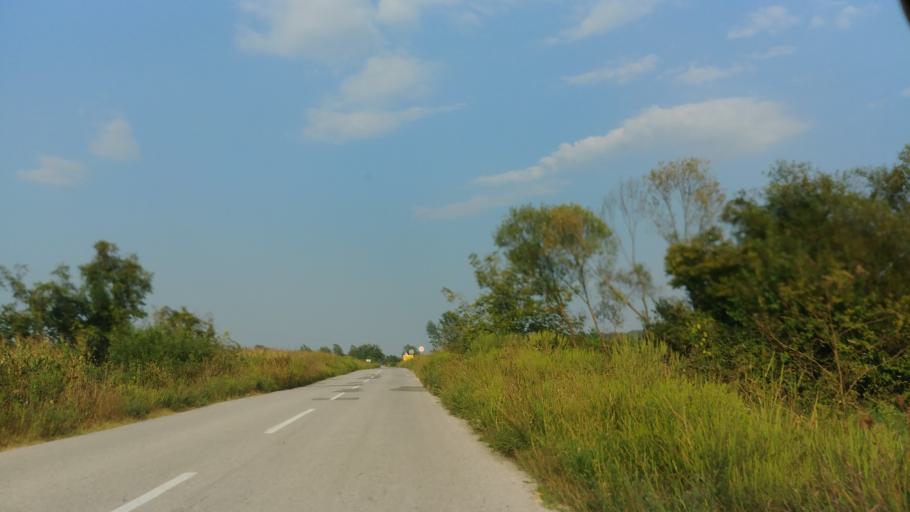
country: BA
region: Republika Srpska
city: Lopare
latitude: 44.7418
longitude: 18.8725
